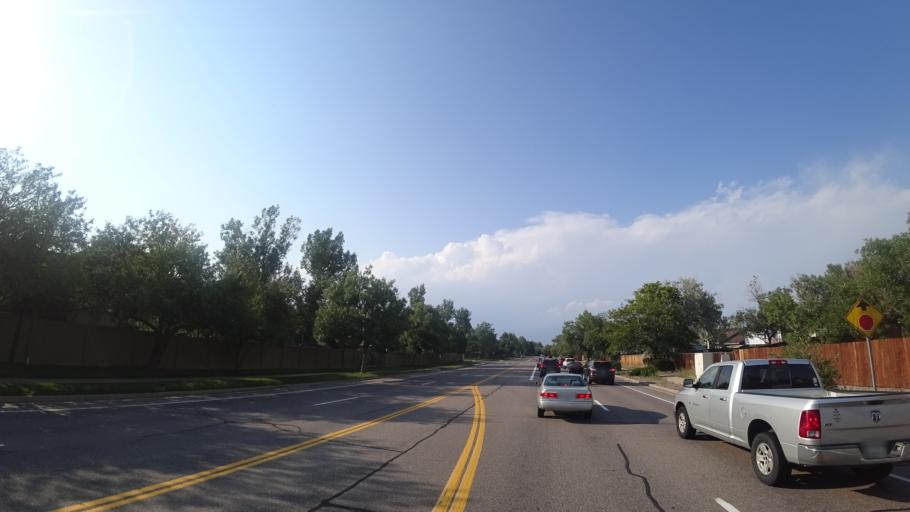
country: US
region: Colorado
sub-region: Arapahoe County
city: Dove Valley
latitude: 39.6105
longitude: -104.7447
